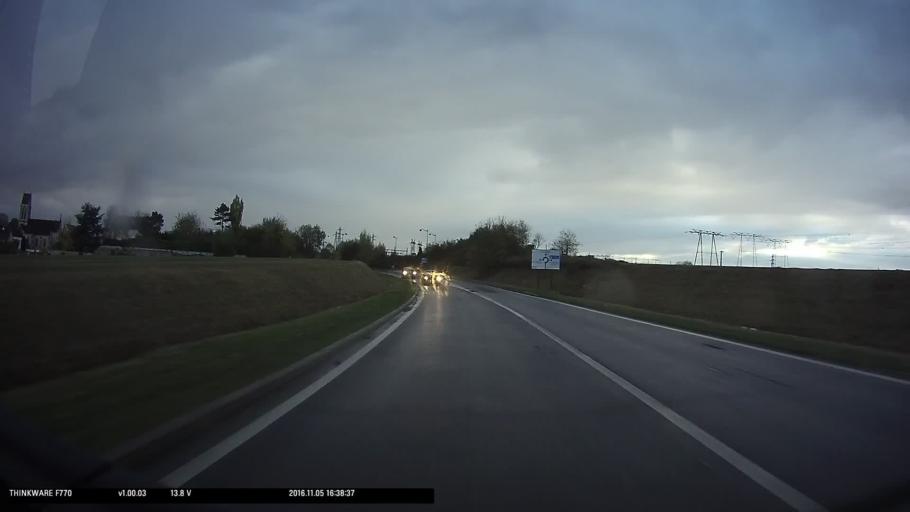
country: FR
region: Ile-de-France
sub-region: Departement du Val-d'Oise
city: Courdimanche
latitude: 49.0592
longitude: 2.0181
